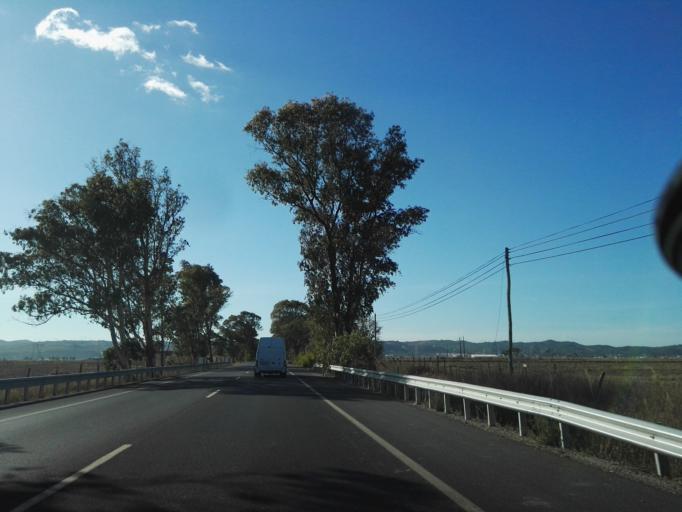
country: PT
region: Lisbon
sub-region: Vila Franca de Xira
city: Vila Franca de Xira
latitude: 38.9402
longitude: -8.9393
